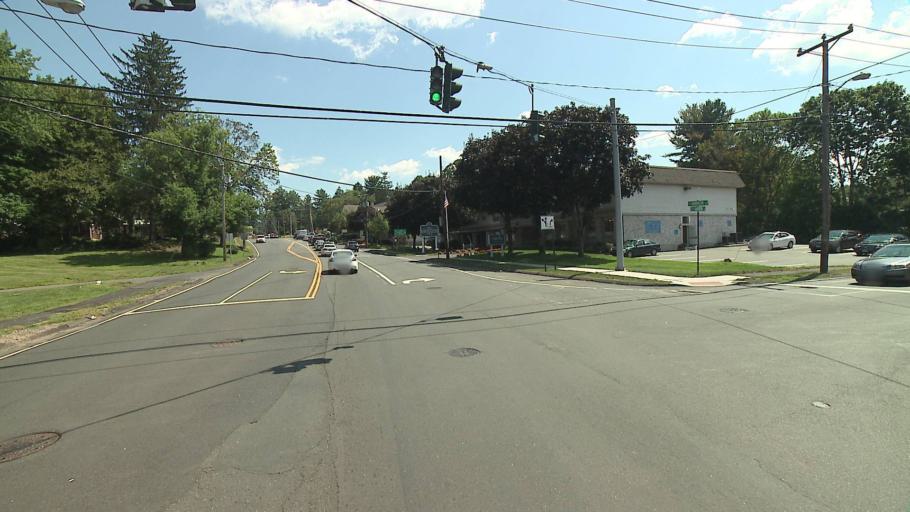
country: US
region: Connecticut
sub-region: Hartford County
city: Farmington
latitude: 41.7274
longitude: -72.8267
